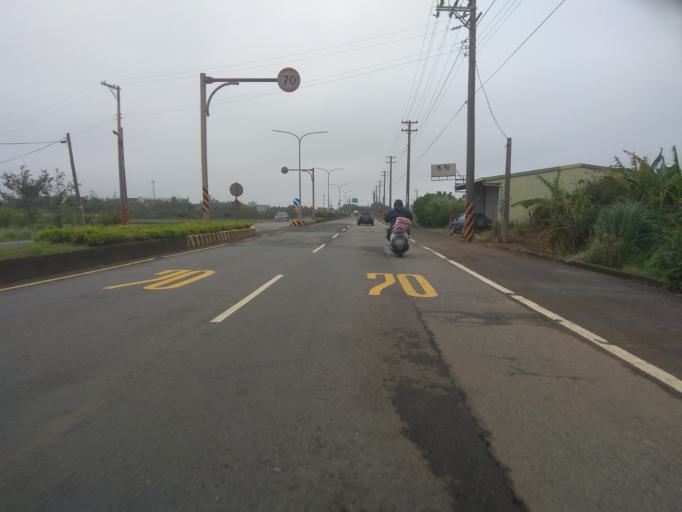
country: TW
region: Taiwan
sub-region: Hsinchu
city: Zhubei
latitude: 25.0121
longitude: 121.0490
